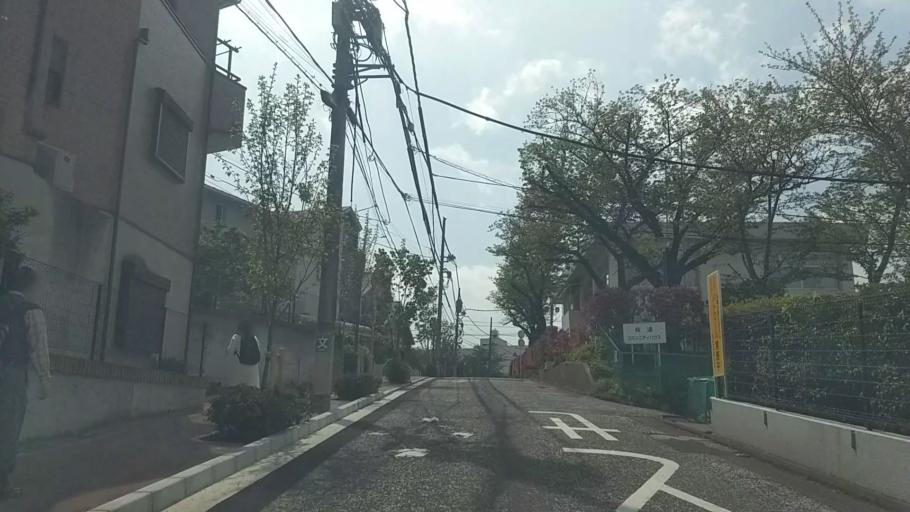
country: JP
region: Kanagawa
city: Yokohama
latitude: 35.3991
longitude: 139.5909
